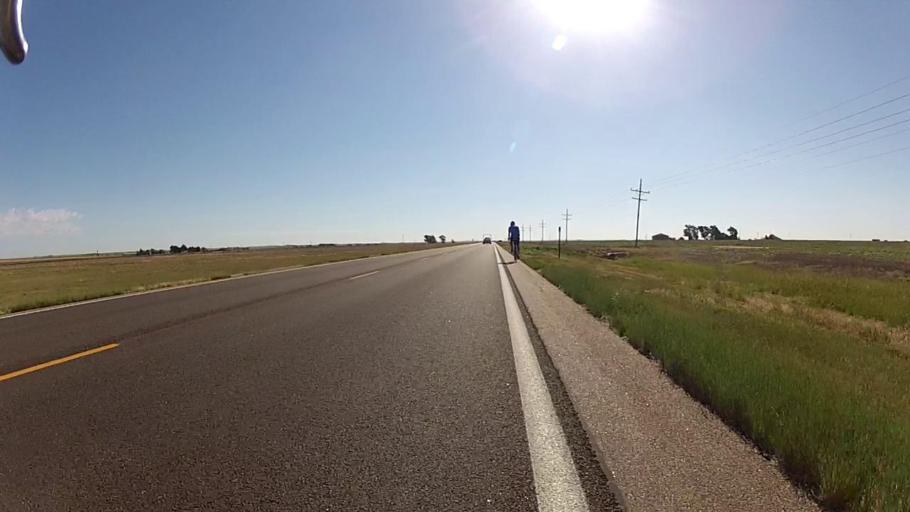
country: US
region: Kansas
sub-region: Haskell County
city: Sublette
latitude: 37.5503
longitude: -100.6027
